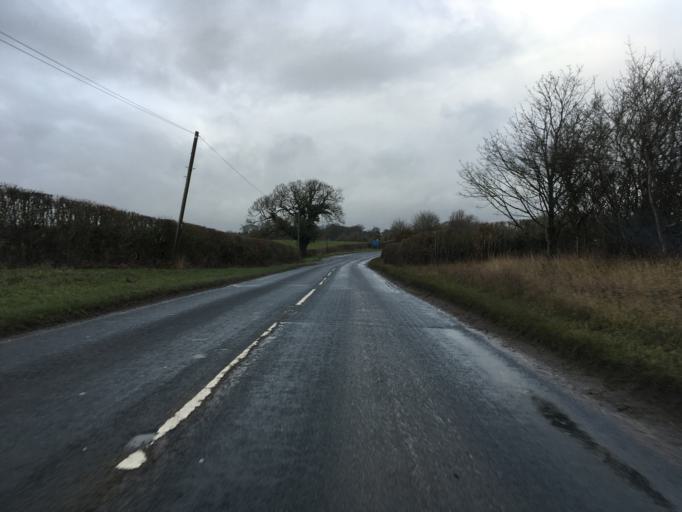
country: GB
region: England
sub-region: Gloucestershire
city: Tetbury
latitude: 51.6210
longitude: -2.1267
